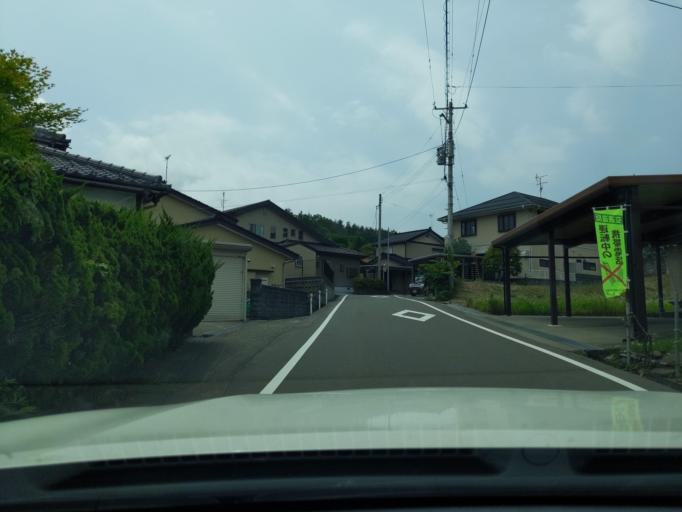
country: JP
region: Niigata
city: Kashiwazaki
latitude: 37.3536
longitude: 138.5472
